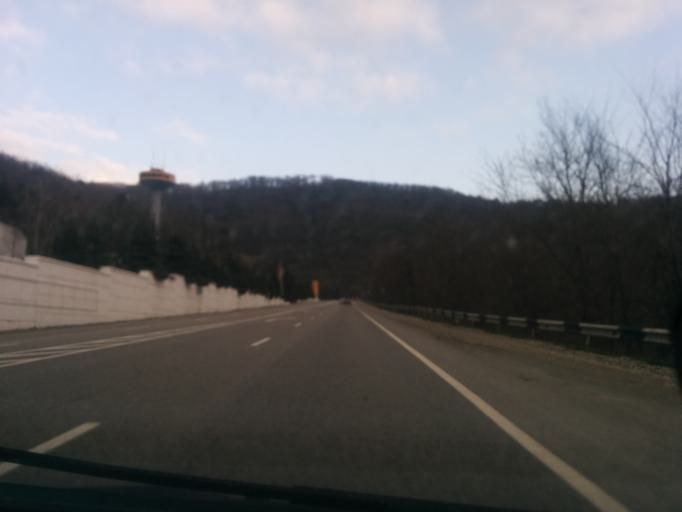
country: RU
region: Krasnodarskiy
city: Agoy
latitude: 44.1416
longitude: 39.0459
